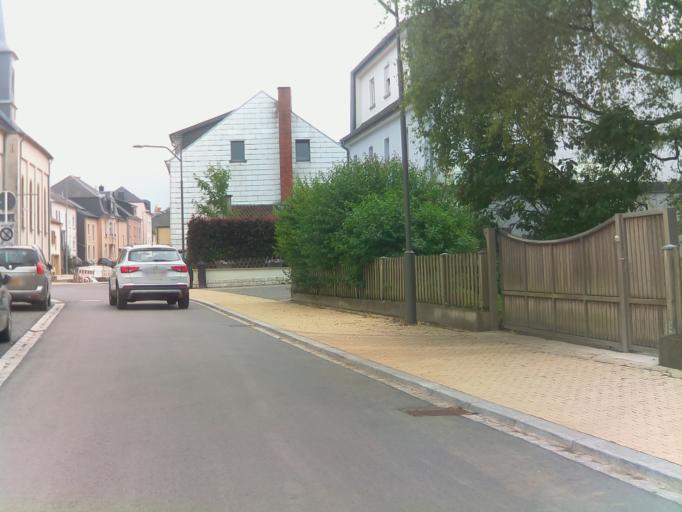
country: LU
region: Luxembourg
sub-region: Canton de Capellen
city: Steinfort
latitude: 49.6458
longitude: 5.9142
